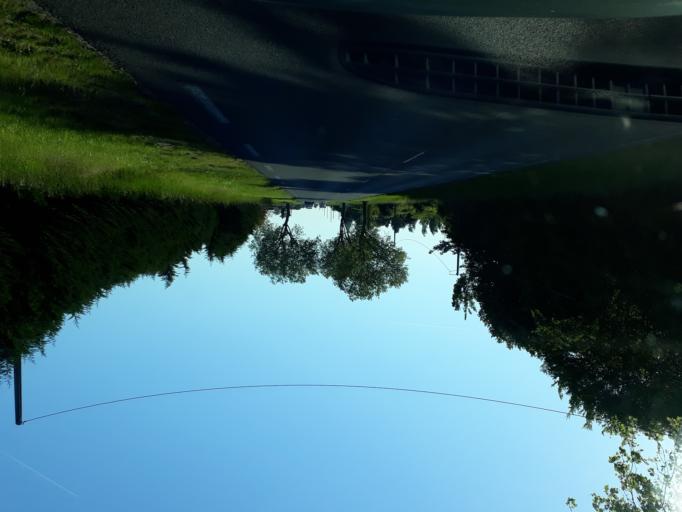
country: FR
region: Centre
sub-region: Departement du Loiret
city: Bonny-sur-Loire
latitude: 47.5863
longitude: 2.8096
